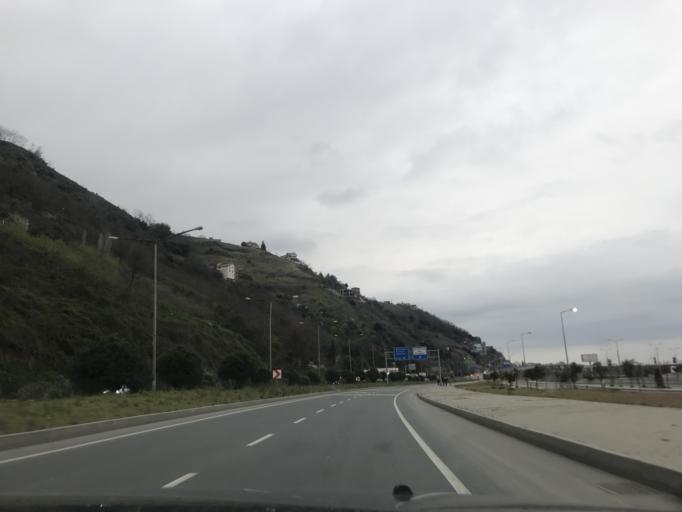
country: TR
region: Trabzon
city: Derecik
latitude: 40.9962
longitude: 39.6455
